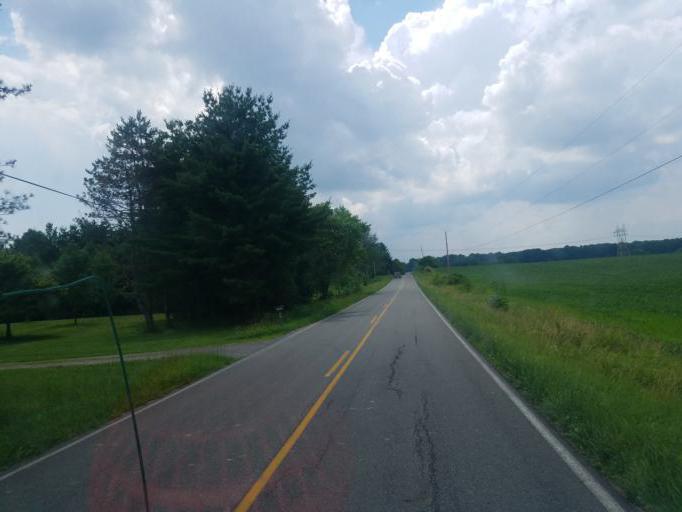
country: US
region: Ohio
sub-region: Columbiana County
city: Salem
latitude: 40.9730
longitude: -80.8374
